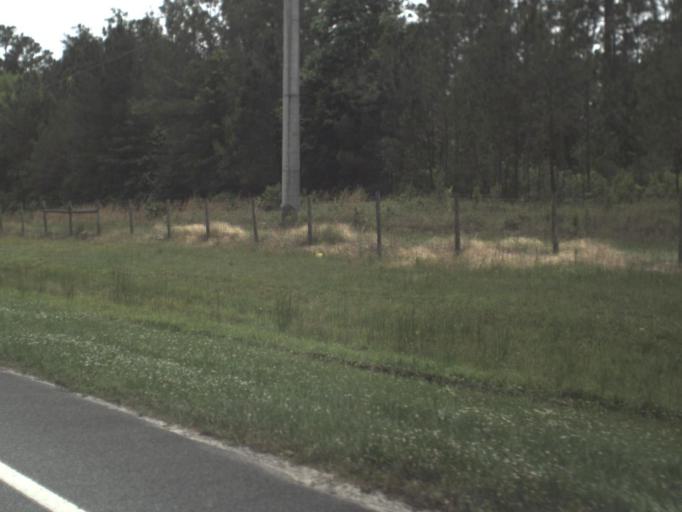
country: US
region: Florida
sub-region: Clay County
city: Middleburg
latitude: 29.9677
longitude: -81.8977
